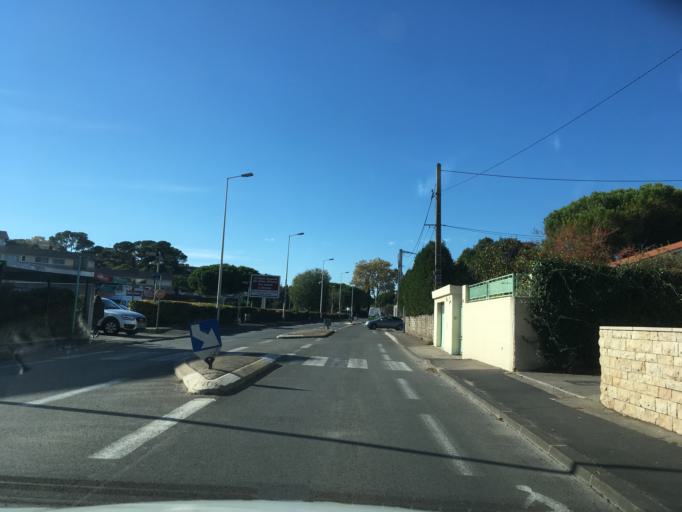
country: FR
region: Languedoc-Roussillon
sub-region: Departement de l'Herault
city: Montpellier
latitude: 43.6017
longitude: 3.8525
